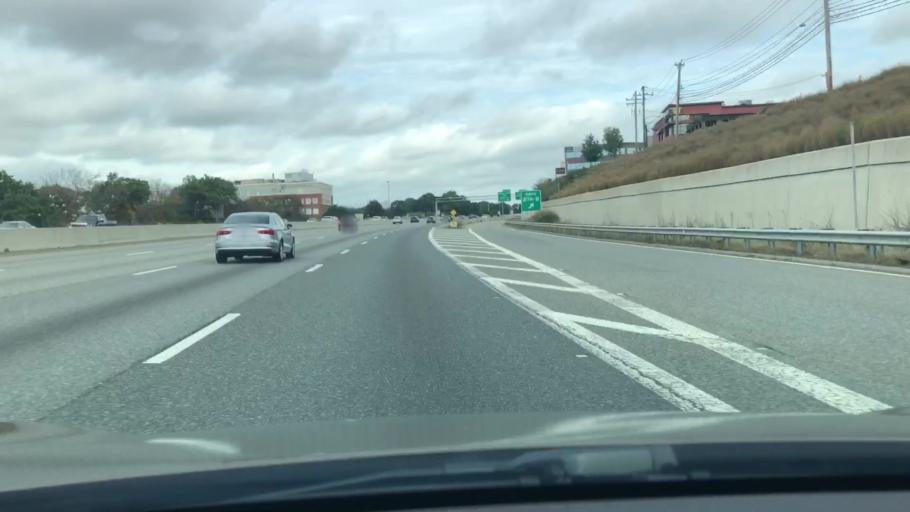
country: US
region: Massachusetts
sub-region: Middlesex County
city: Waltham
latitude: 42.3923
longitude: -71.2622
